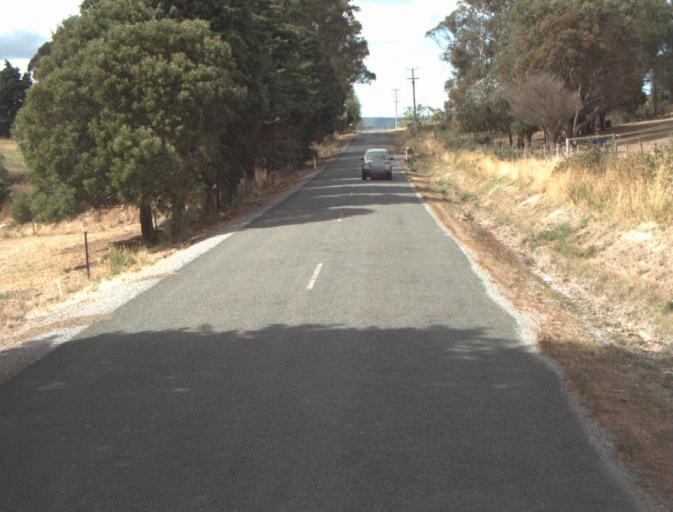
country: AU
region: Tasmania
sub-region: Launceston
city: Mayfield
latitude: -41.2153
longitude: 147.1357
